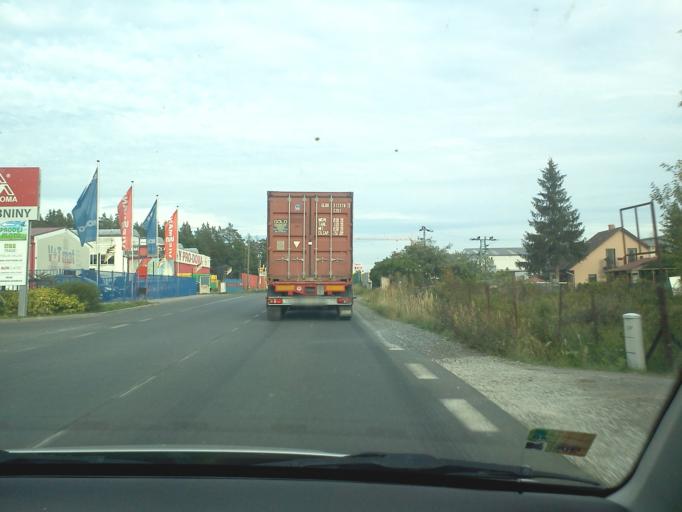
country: CZ
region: Central Bohemia
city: Mukarov
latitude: 49.9900
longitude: 14.7246
